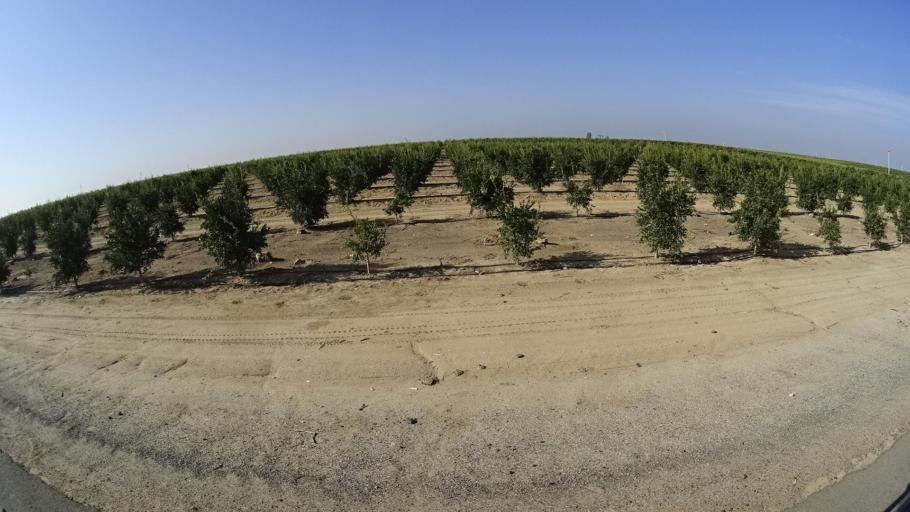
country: US
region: California
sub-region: Kern County
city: McFarland
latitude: 35.6052
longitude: -119.1688
